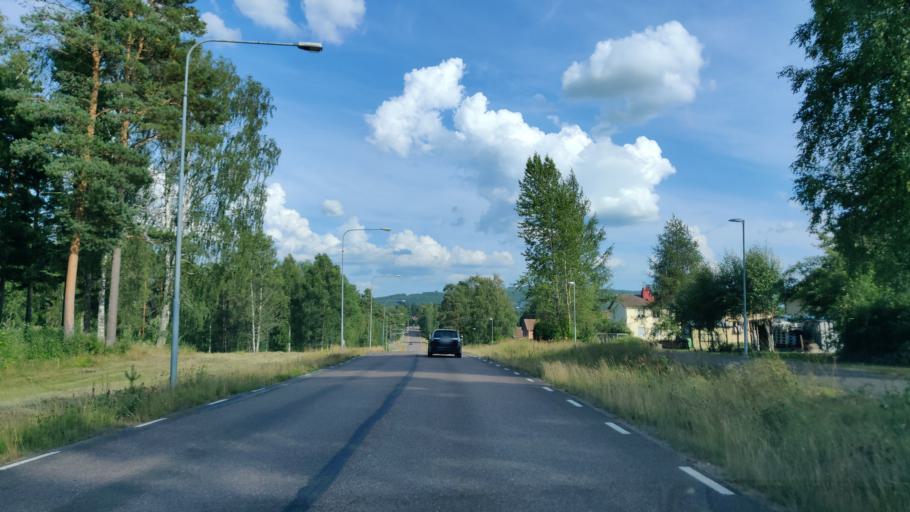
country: SE
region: Vaermland
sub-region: Hagfors Kommun
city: Hagfors
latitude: 60.0463
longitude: 13.6757
